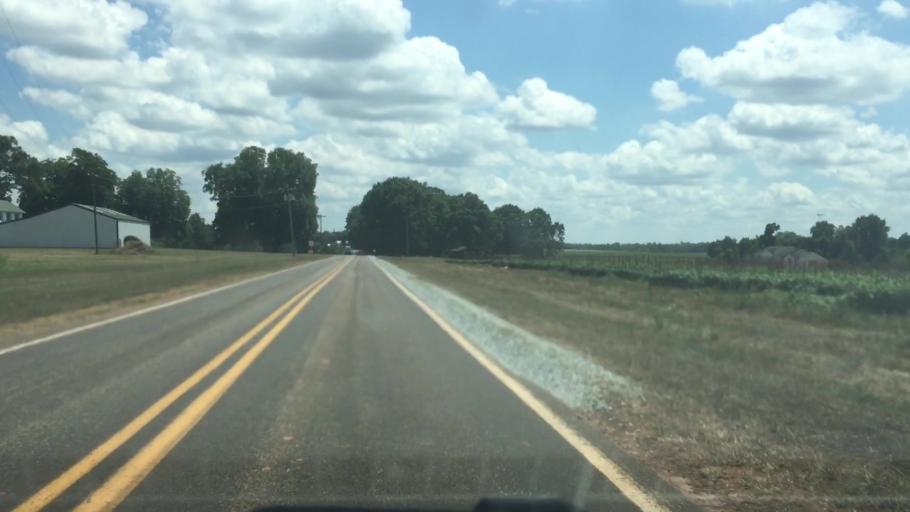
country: US
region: North Carolina
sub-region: Rowan County
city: Landis
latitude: 35.6427
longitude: -80.6684
